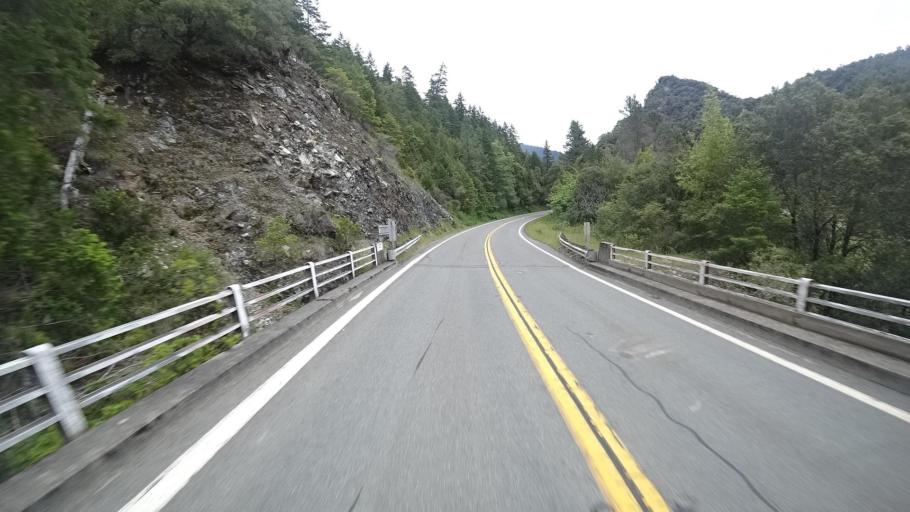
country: US
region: California
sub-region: Humboldt County
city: Willow Creek
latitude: 41.2293
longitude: -123.6595
